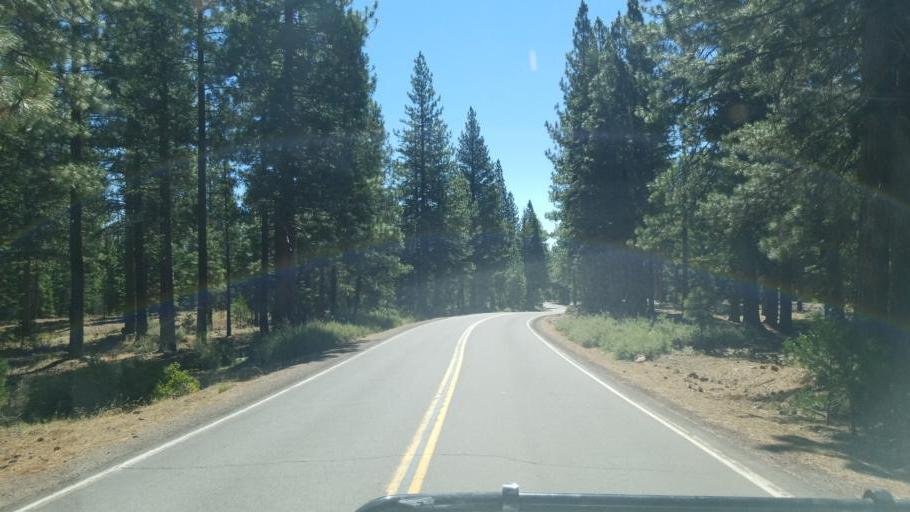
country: US
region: California
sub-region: Lassen County
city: Susanville
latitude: 40.4361
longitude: -120.7427
